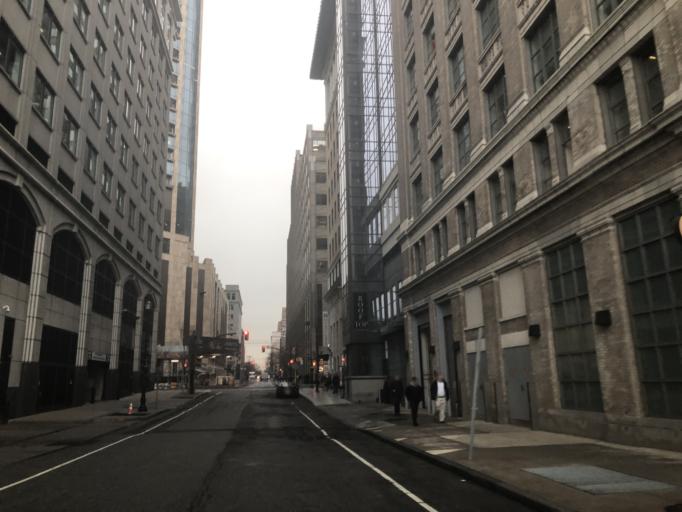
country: US
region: New York
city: New York City
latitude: 40.7155
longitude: -74.0332
